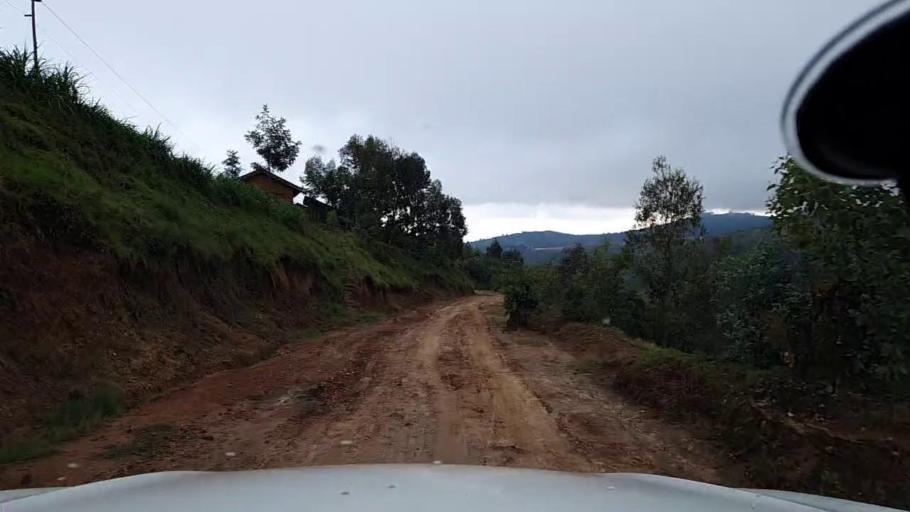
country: RW
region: Western Province
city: Kibuye
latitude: -2.0874
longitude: 29.5030
